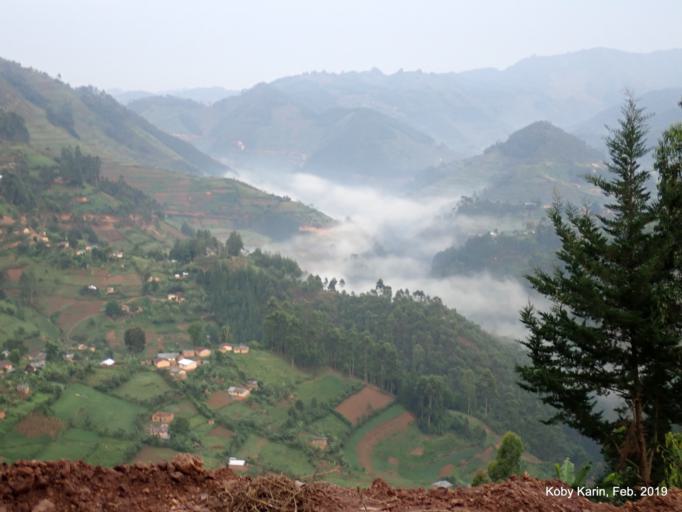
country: UG
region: Western Region
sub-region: Kisoro District
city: Kisoro
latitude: -1.1339
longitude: 29.7311
